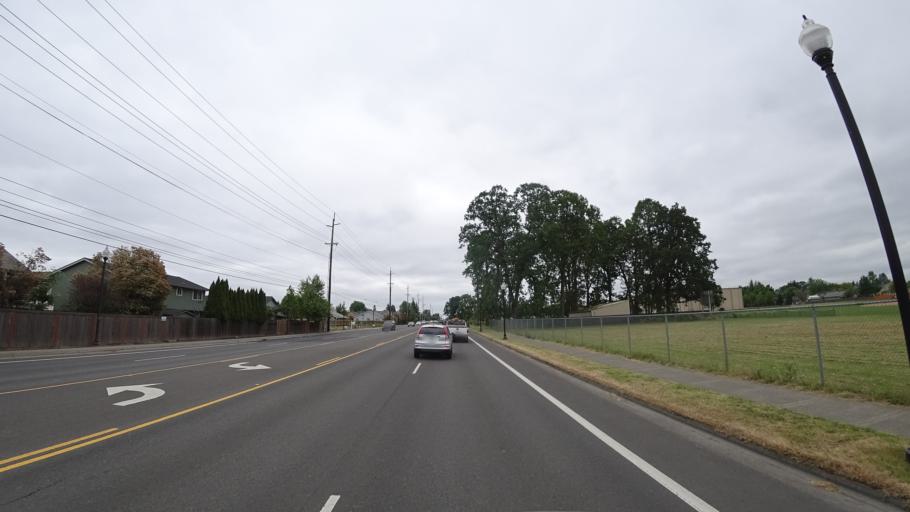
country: US
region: Oregon
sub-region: Washington County
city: Aloha
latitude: 45.5116
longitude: -122.9021
